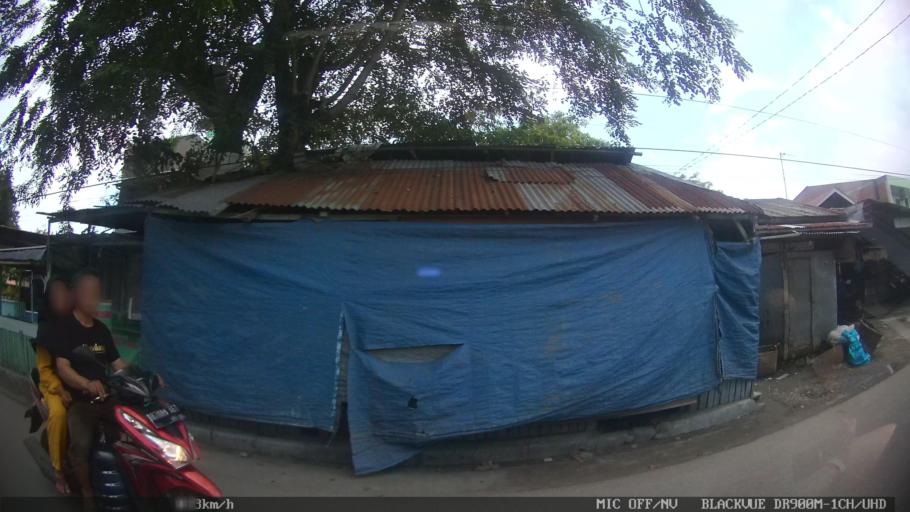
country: ID
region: North Sumatra
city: Labuhan Deli
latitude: 3.6881
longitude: 98.6925
